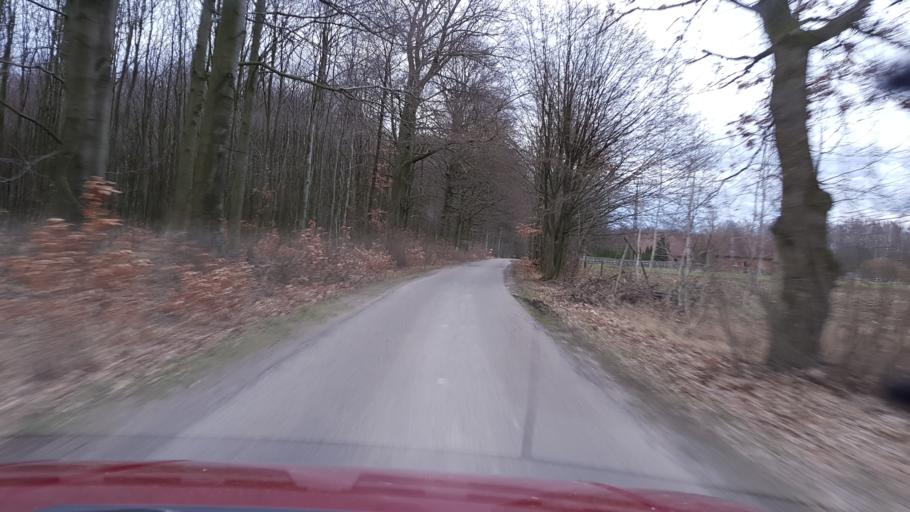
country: PL
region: West Pomeranian Voivodeship
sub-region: Powiat gryfinski
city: Stare Czarnowo
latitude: 53.3235
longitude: 14.7043
